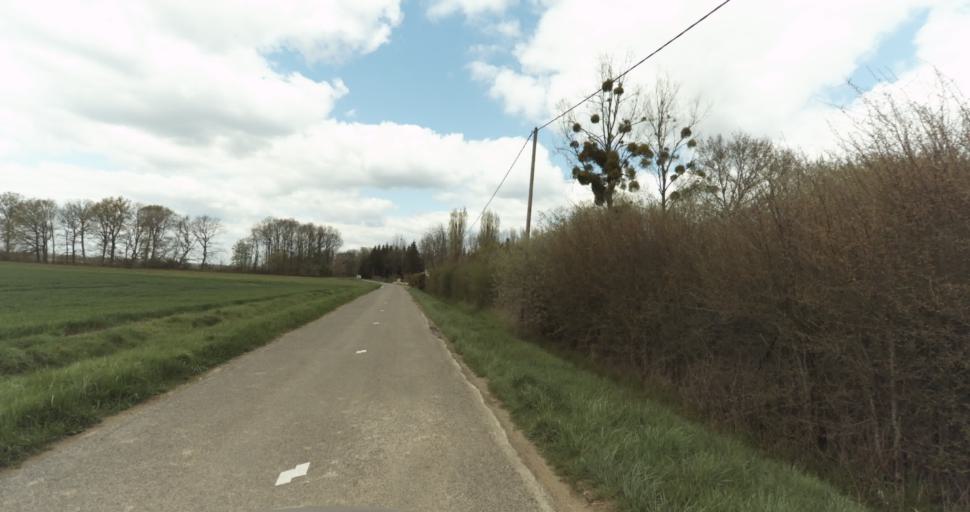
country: FR
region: Bourgogne
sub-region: Departement de la Cote-d'Or
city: Auxonne
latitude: 47.1795
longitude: 5.4195
